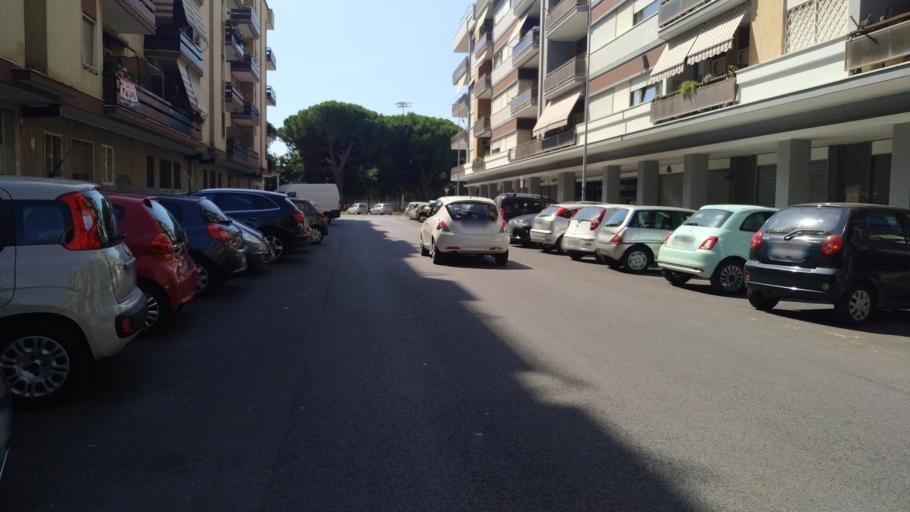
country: IT
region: Latium
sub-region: Citta metropolitana di Roma Capitale
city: Lido di Ostia
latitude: 41.7332
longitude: 12.3021
